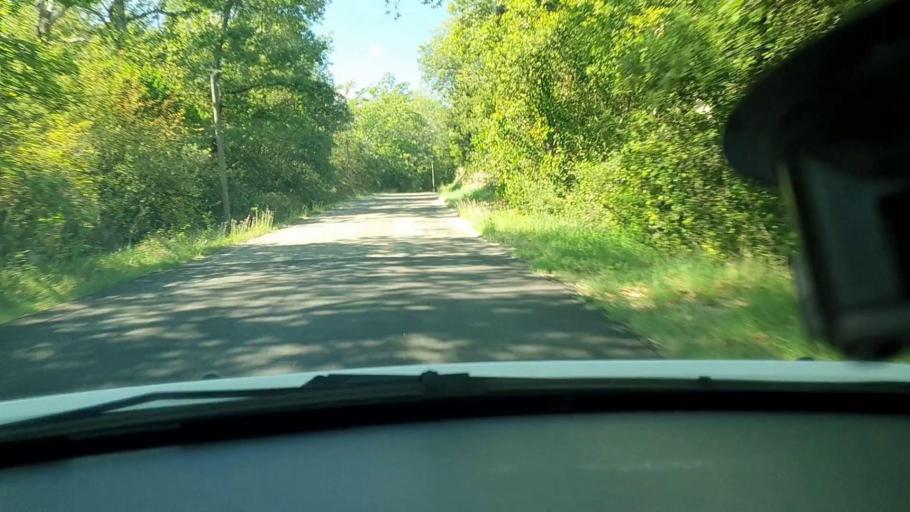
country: FR
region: Languedoc-Roussillon
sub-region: Departement du Gard
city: Sabran
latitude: 44.1748
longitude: 4.5071
